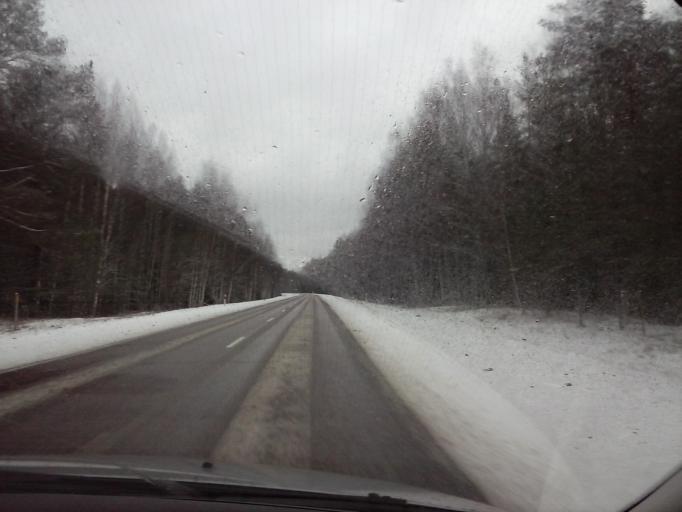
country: LV
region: Strenci
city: Seda
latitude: 57.6340
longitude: 25.8209
